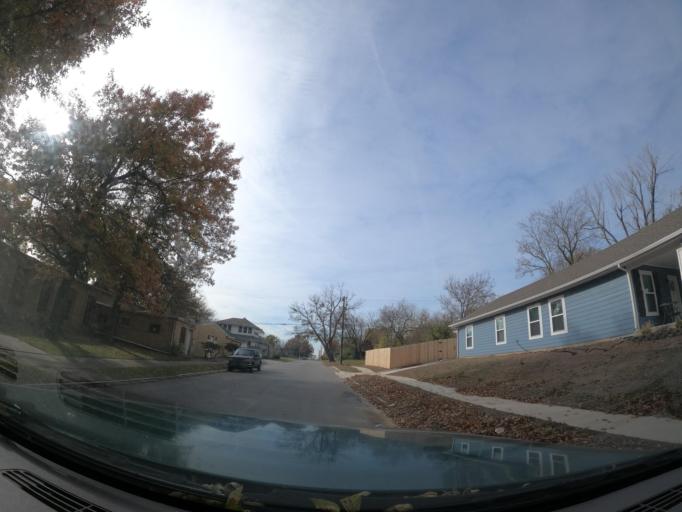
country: US
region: Oklahoma
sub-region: Tulsa County
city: Tulsa
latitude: 36.1627
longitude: -95.9634
